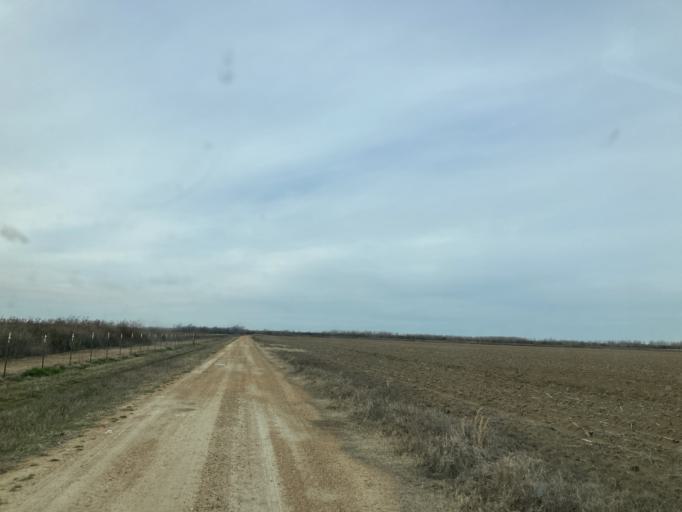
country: US
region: Mississippi
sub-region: Humphreys County
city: Belzoni
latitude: 33.1236
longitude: -90.6173
